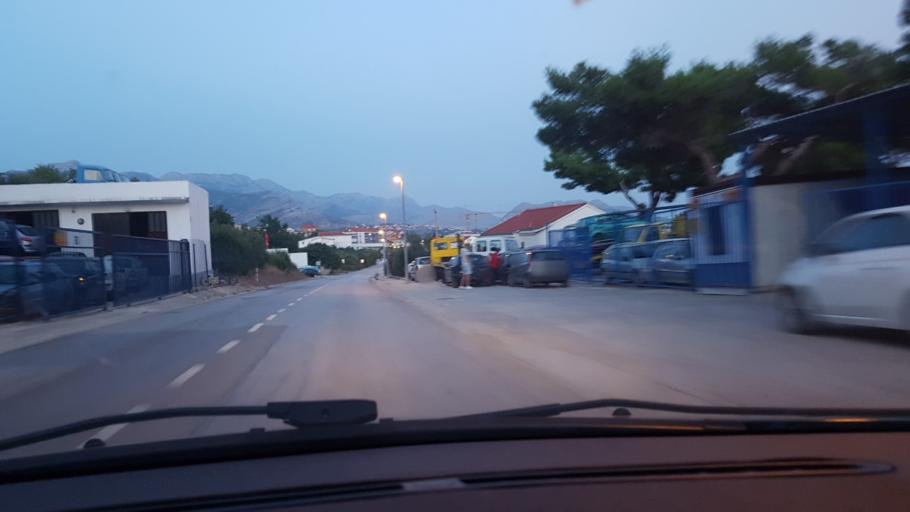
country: HR
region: Splitsko-Dalmatinska
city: Vranjic
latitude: 43.5449
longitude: 16.4657
